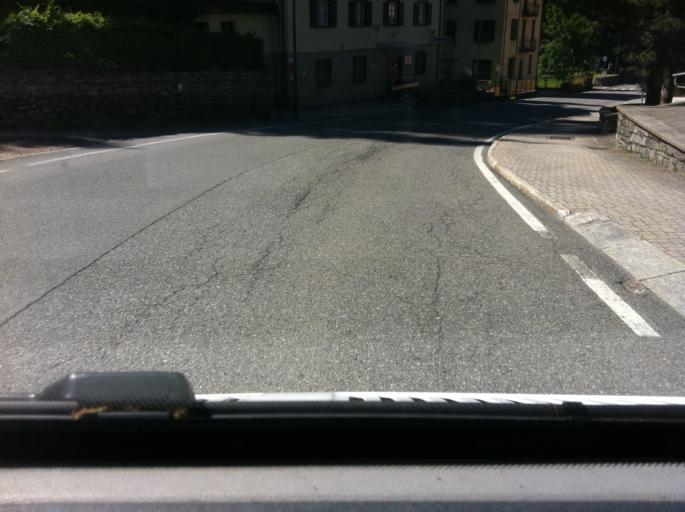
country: IT
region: Lombardy
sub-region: Provincia di Sondrio
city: Campodolcino
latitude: 46.4178
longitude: 9.3418
